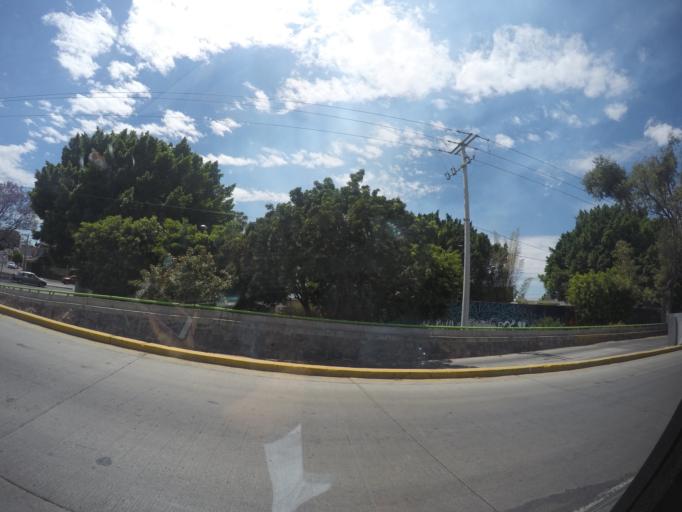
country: MX
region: Guanajuato
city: Leon
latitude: 21.1090
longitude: -101.6632
